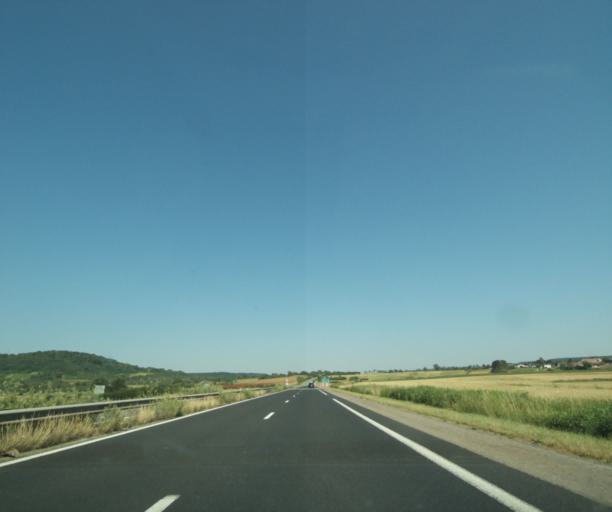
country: FR
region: Lorraine
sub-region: Departement de Meurthe-et-Moselle
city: Domgermain
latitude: 48.6472
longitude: 5.8500
